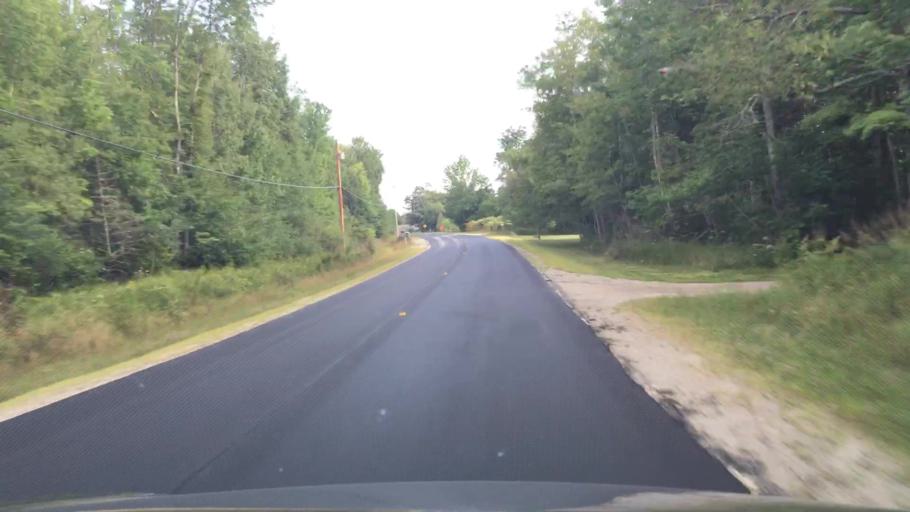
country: US
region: Maine
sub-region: Hancock County
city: Orland
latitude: 44.5489
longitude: -68.6208
